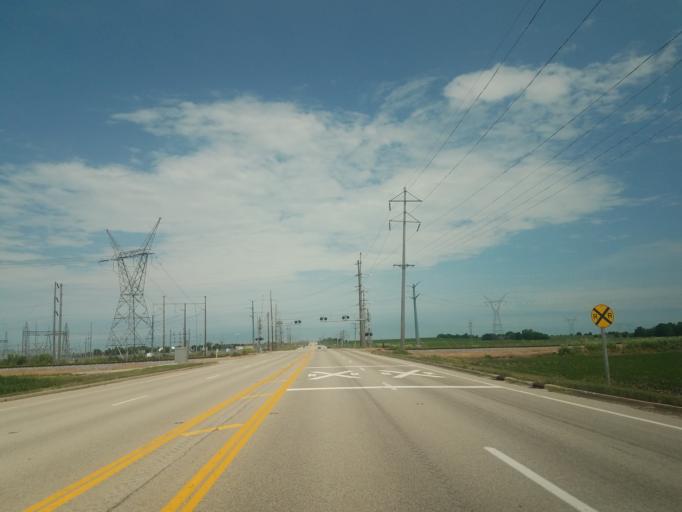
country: US
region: Illinois
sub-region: McLean County
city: Downs
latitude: 40.4502
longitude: -88.9017
